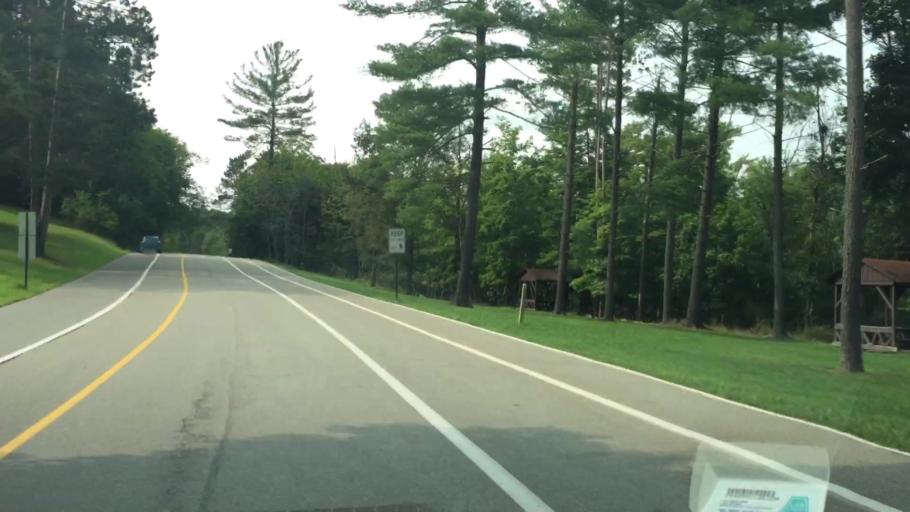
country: US
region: Pennsylvania
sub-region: Allegheny County
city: Gibsonia
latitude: 40.5972
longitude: -80.0005
